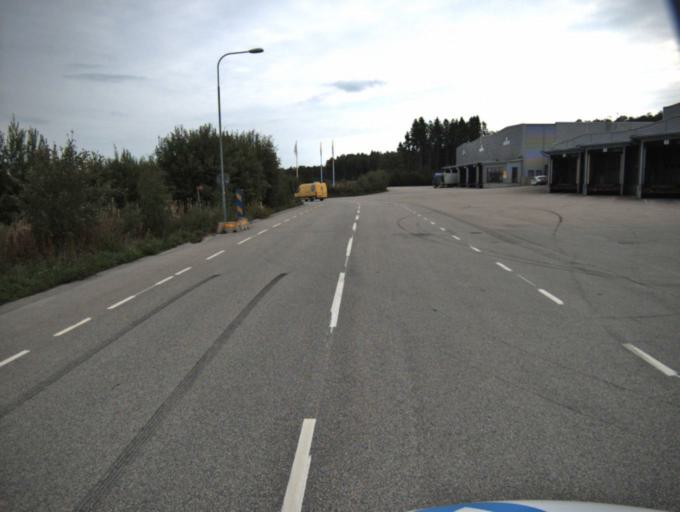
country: SE
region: Vaestra Goetaland
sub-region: Ulricehamns Kommun
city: Ulricehamn
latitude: 57.8007
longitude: 13.4460
